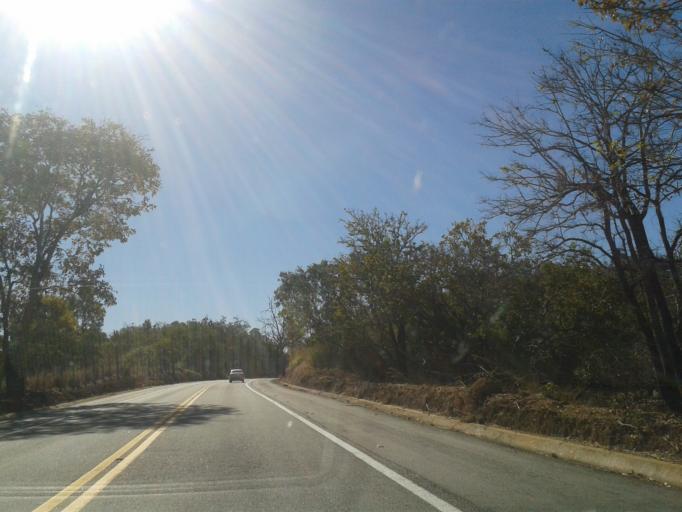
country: BR
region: Goias
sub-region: Goias
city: Goias
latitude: -15.6699
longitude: -50.2146
